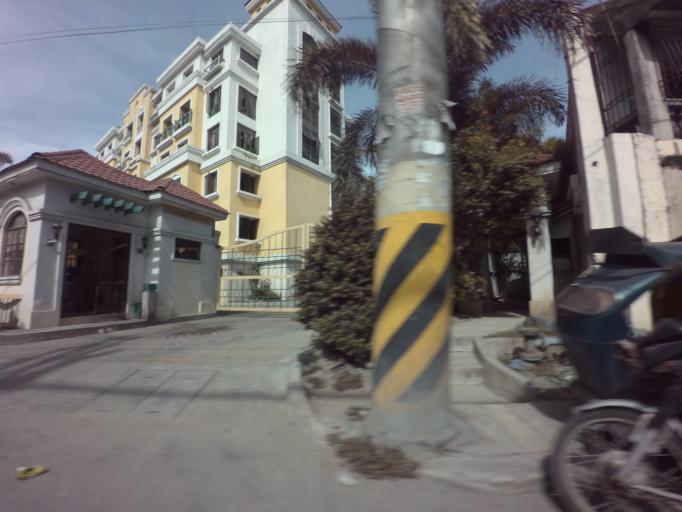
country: PH
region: Calabarzon
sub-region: Province of Rizal
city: Pateros
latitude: 14.5474
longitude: 121.0876
